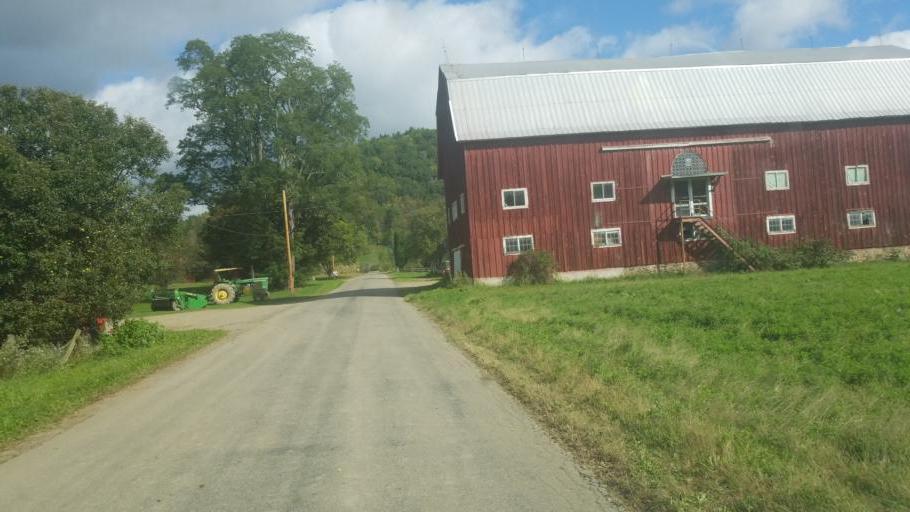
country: US
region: New York
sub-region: Cattaraugus County
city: Weston Mills
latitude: 42.1337
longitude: -78.3442
